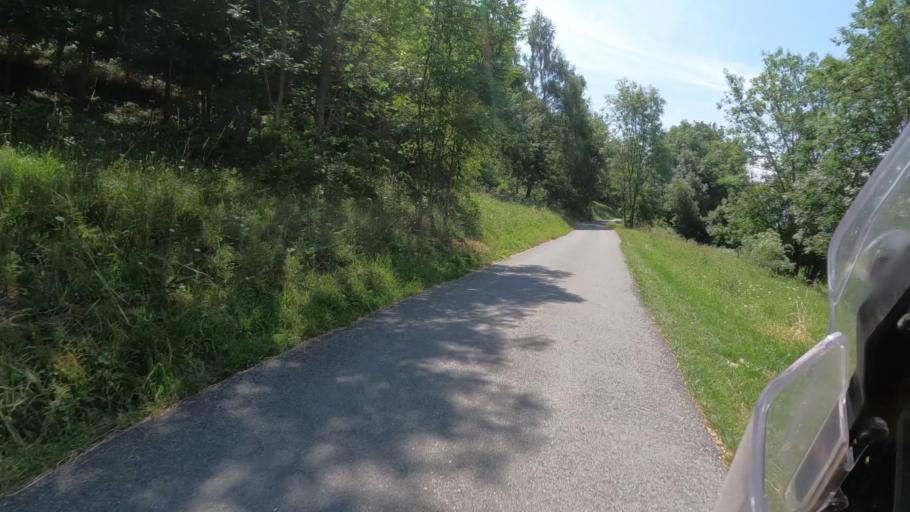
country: IT
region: Piedmont
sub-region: Provincia di Torino
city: Sant'Antonino di Susa
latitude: 45.1516
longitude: 7.2720
